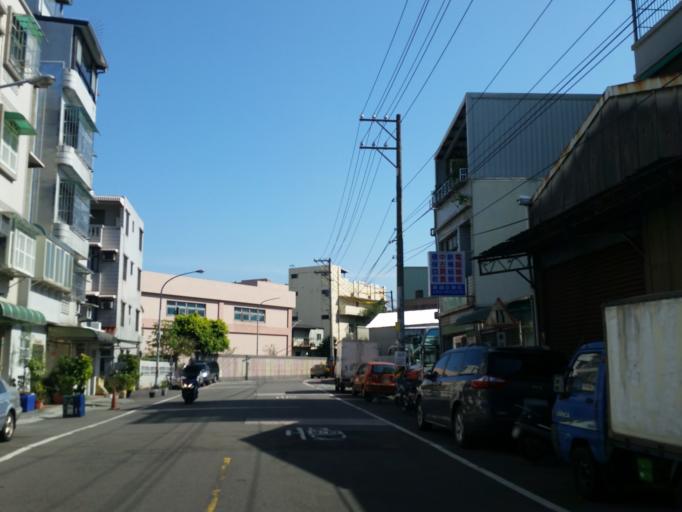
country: TW
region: Taiwan
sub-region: Taoyuan
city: Taoyuan
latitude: 24.9875
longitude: 121.3207
